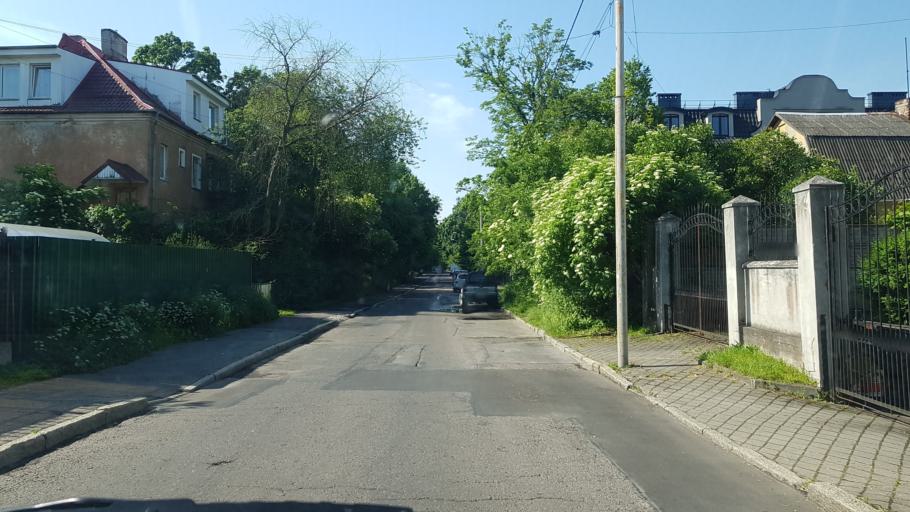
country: RU
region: Kaliningrad
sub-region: Gorod Kaliningrad
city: Kaliningrad
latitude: 54.7194
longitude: 20.4577
